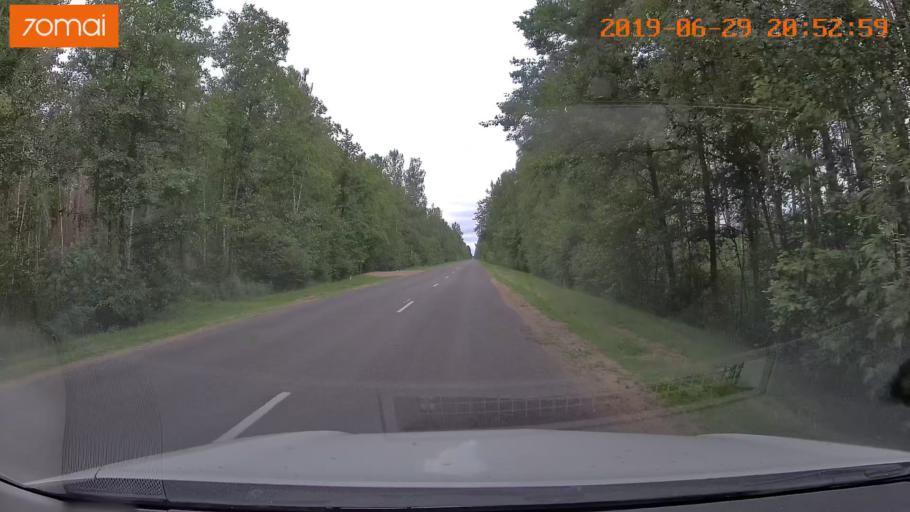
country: BY
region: Brest
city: Hantsavichy
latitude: 52.6999
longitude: 26.3634
